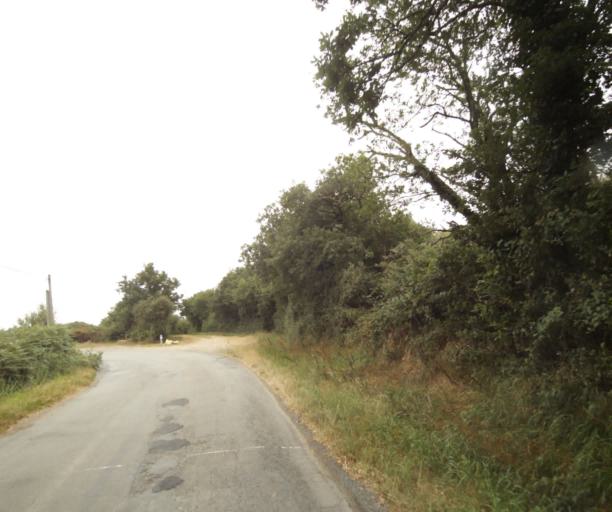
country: FR
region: Pays de la Loire
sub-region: Departement de la Vendee
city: Chateau-d'Olonne
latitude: 46.4807
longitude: -1.6877
